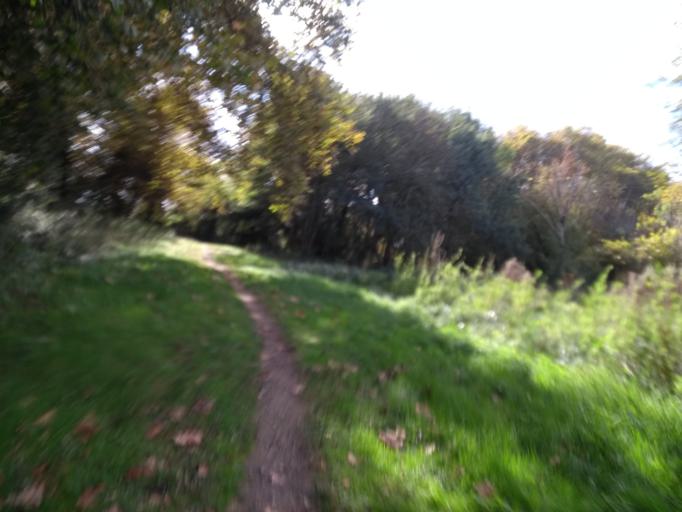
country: FR
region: Aquitaine
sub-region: Departement de la Gironde
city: Gradignan
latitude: 44.7740
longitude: -0.5932
